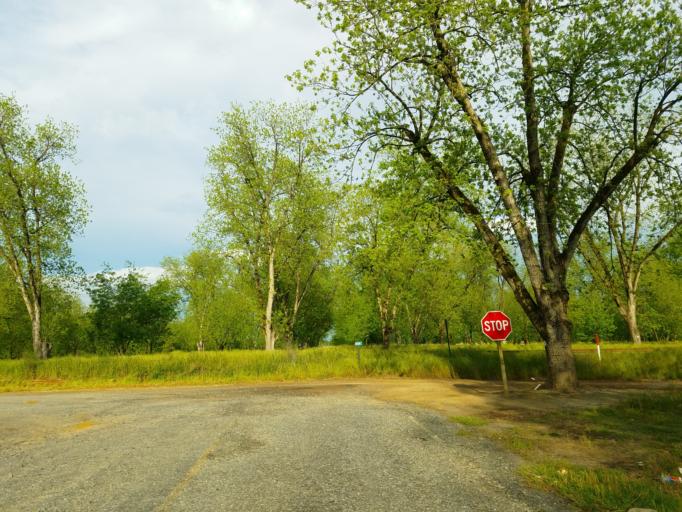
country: US
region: Georgia
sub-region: Dooly County
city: Vienna
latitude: 32.0420
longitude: -83.7867
